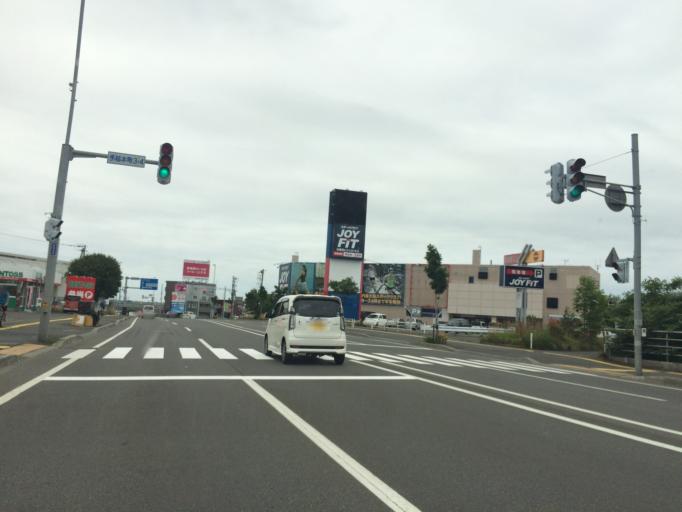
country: JP
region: Hokkaido
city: Sapporo
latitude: 43.1200
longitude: 141.2374
